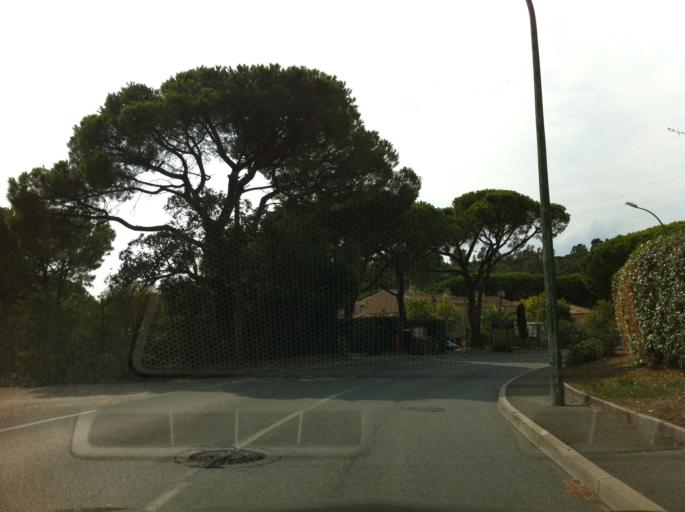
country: FR
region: Provence-Alpes-Cote d'Azur
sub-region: Departement du Var
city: Sainte-Maxime
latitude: 43.3454
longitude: 6.6779
